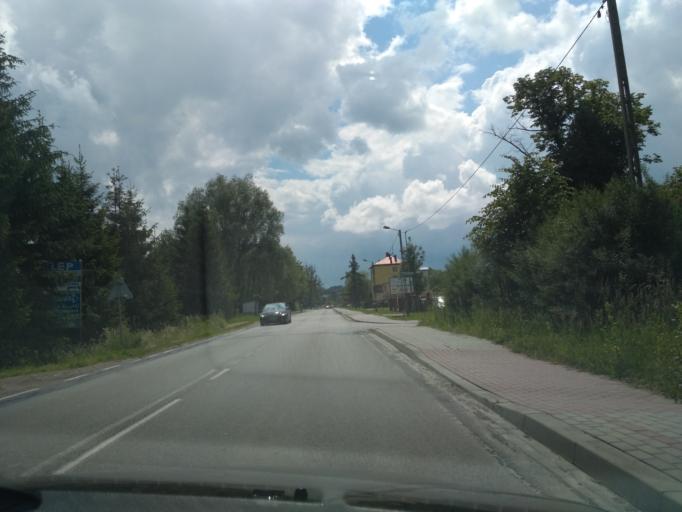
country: PL
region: Subcarpathian Voivodeship
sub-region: Powiat rzeszowski
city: Hyzne
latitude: 49.9264
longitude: 22.1614
